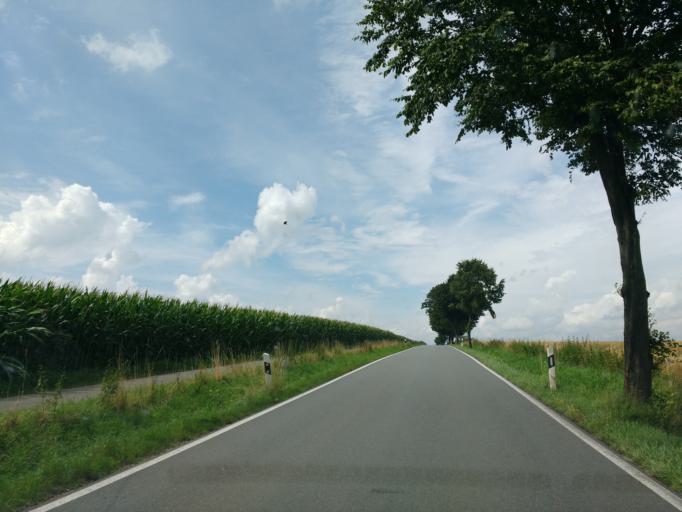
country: DE
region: North Rhine-Westphalia
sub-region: Regierungsbezirk Detmold
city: Steinheim
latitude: 51.8830
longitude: 9.0761
